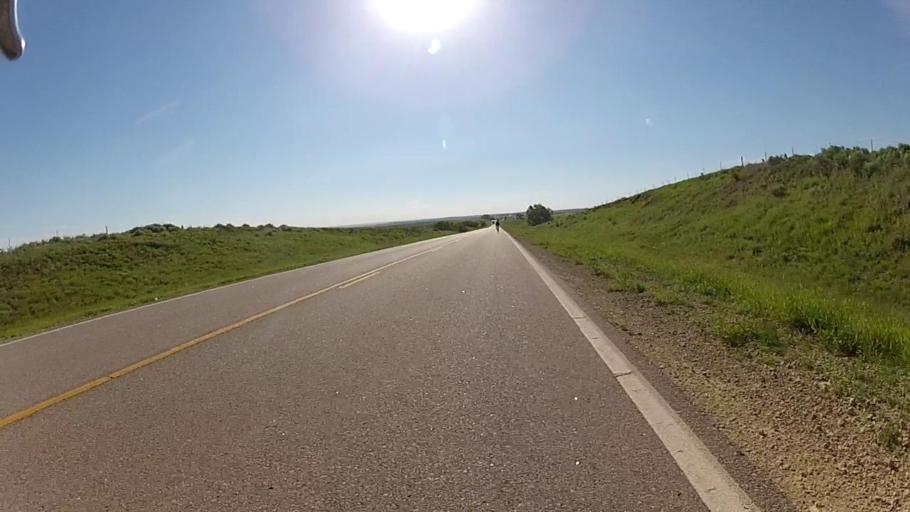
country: US
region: Kansas
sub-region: Barber County
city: Medicine Lodge
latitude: 37.2816
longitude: -98.8968
